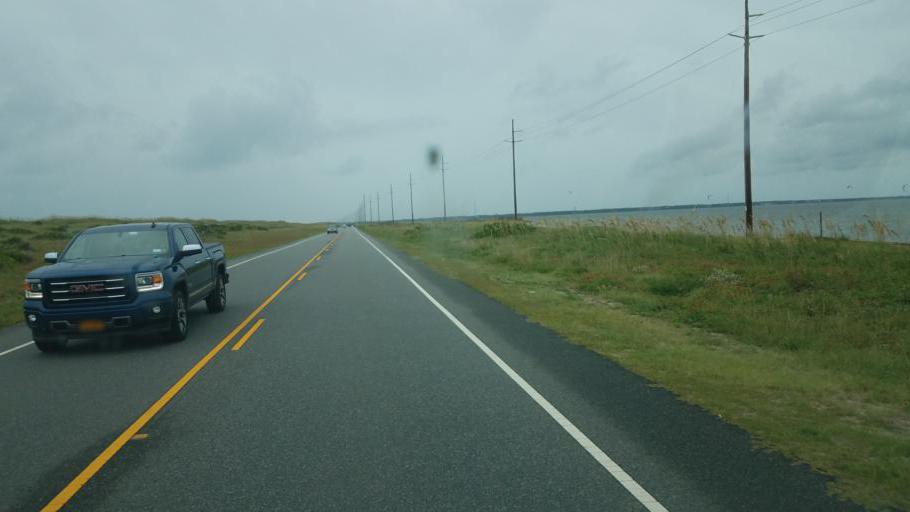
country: US
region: North Carolina
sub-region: Dare County
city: Buxton
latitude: 35.2967
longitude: -75.5139
